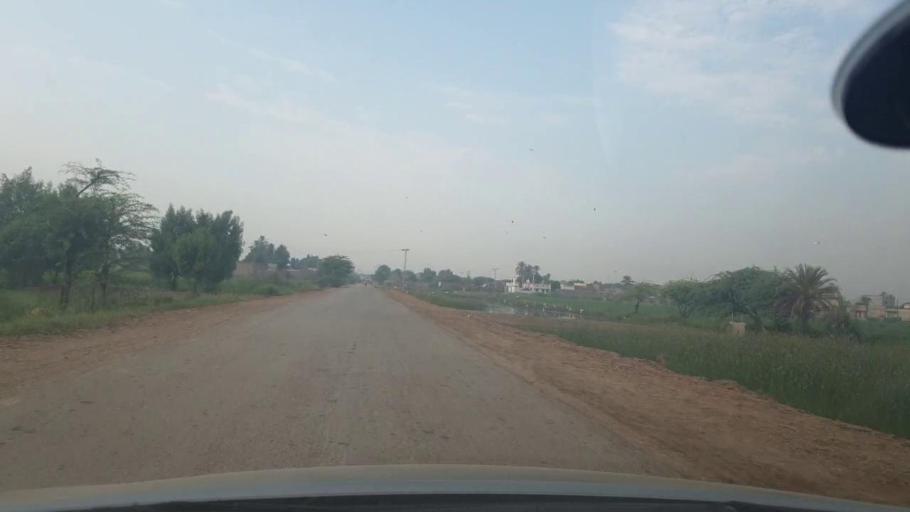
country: PK
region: Sindh
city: Jacobabad
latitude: 28.2707
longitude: 68.4209
